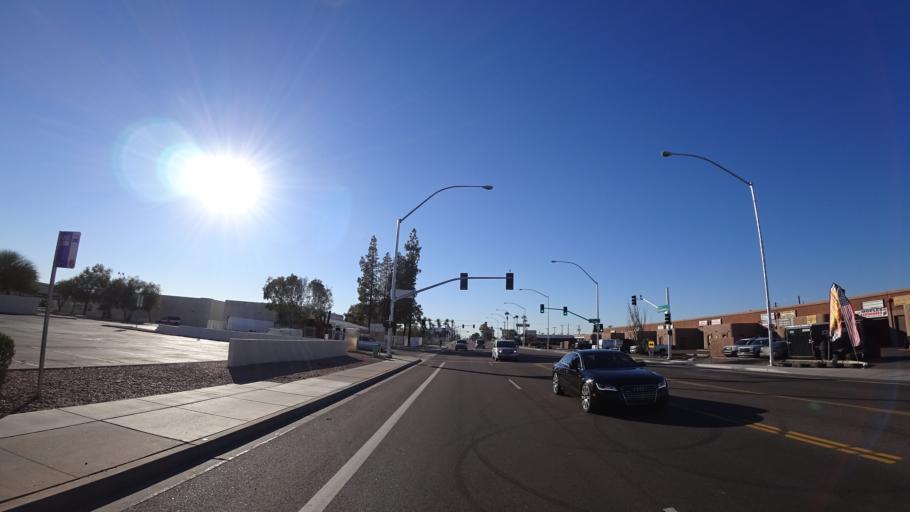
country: US
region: Arizona
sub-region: Maricopa County
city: Mesa
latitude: 33.3932
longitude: -111.8293
